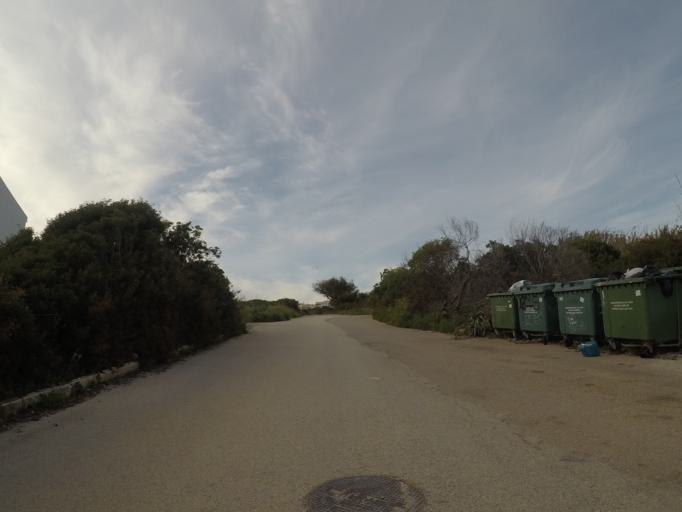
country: PT
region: Faro
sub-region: Lagos
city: Lagos
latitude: 37.0843
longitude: -8.7352
